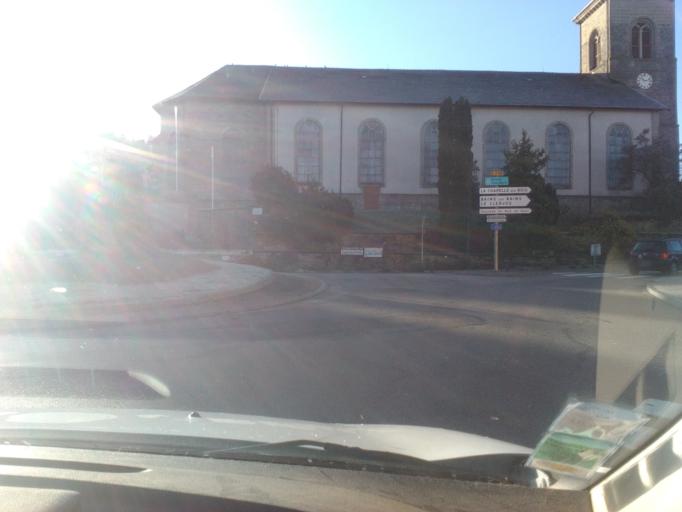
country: FR
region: Lorraine
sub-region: Departement des Vosges
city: Xertigny
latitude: 48.0451
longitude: 6.4023
